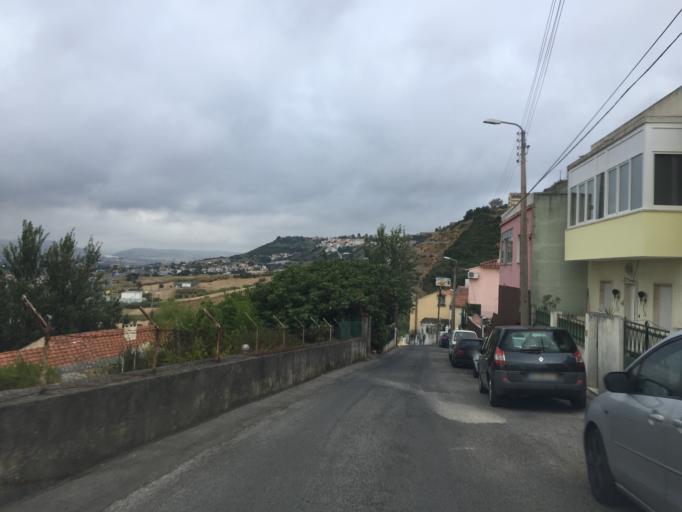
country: PT
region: Lisbon
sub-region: Odivelas
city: Olival do Basto
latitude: 38.7958
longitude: -9.1561
